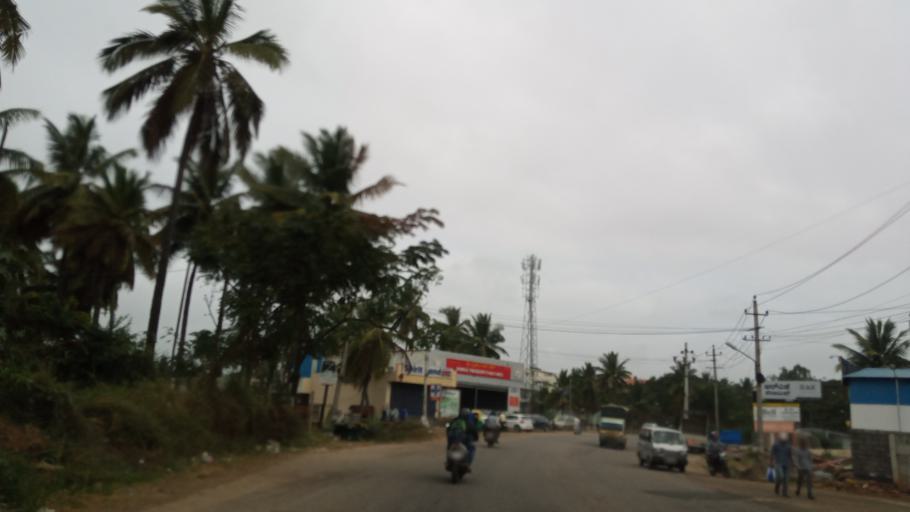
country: IN
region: Karnataka
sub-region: Bangalore Urban
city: Bangalore
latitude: 12.9082
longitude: 77.4875
